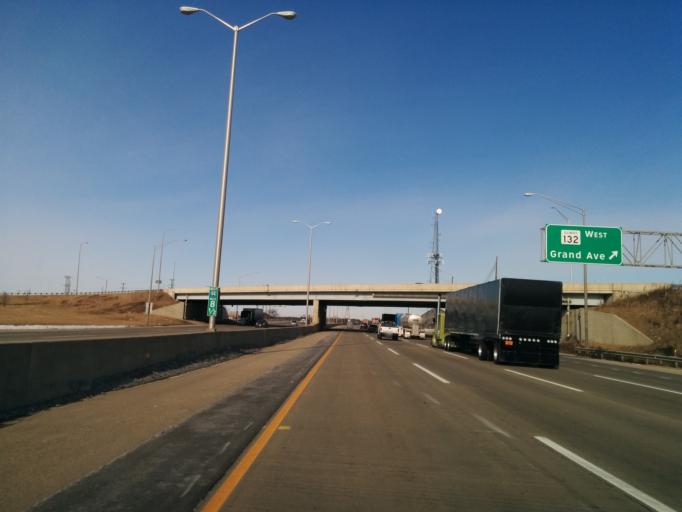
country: US
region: Illinois
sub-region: Lake County
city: Grandwood Park
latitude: 42.3800
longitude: -87.9469
